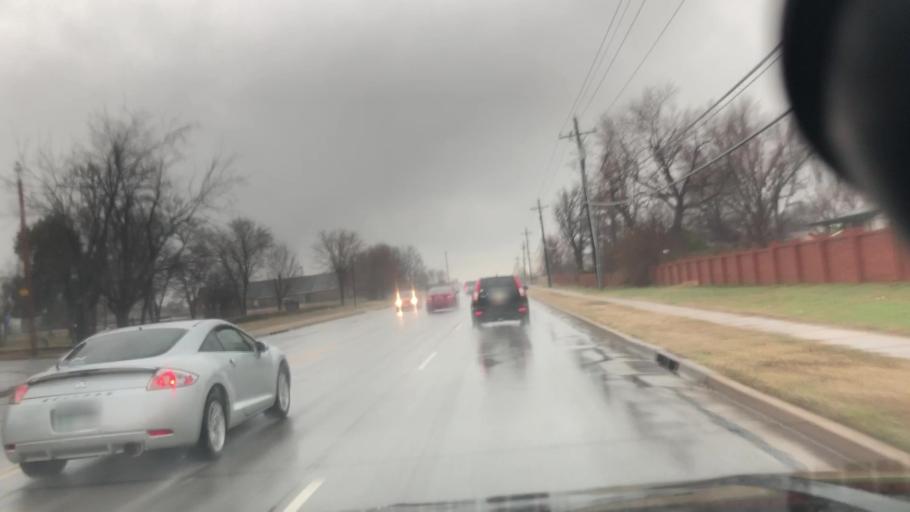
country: US
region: Oklahoma
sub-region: Rogers County
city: Catoosa
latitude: 36.1429
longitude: -95.8333
